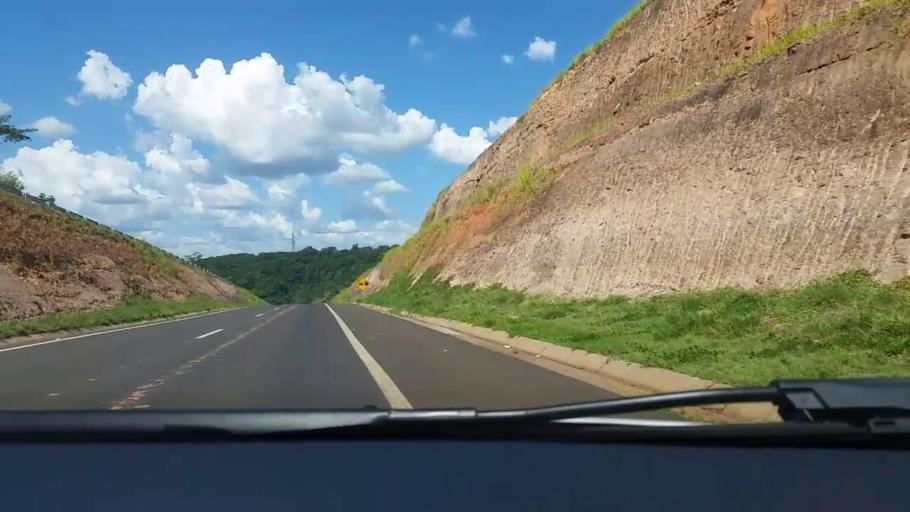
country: BR
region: Sao Paulo
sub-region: Bauru
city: Bauru
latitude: -22.4375
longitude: -49.1393
